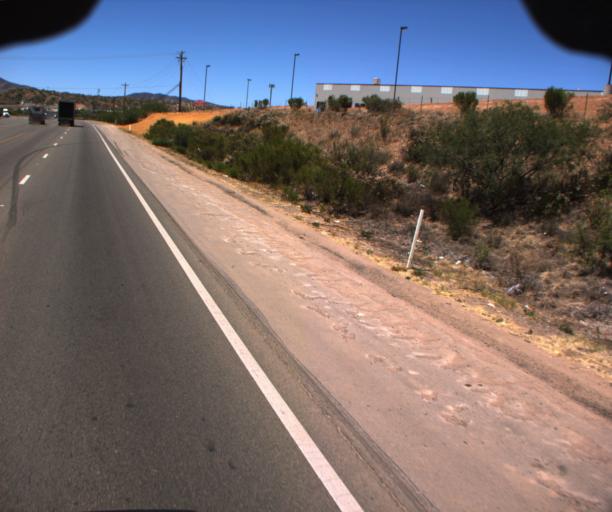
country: US
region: Arizona
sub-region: Santa Cruz County
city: Nogales
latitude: 31.3585
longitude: -110.9577
